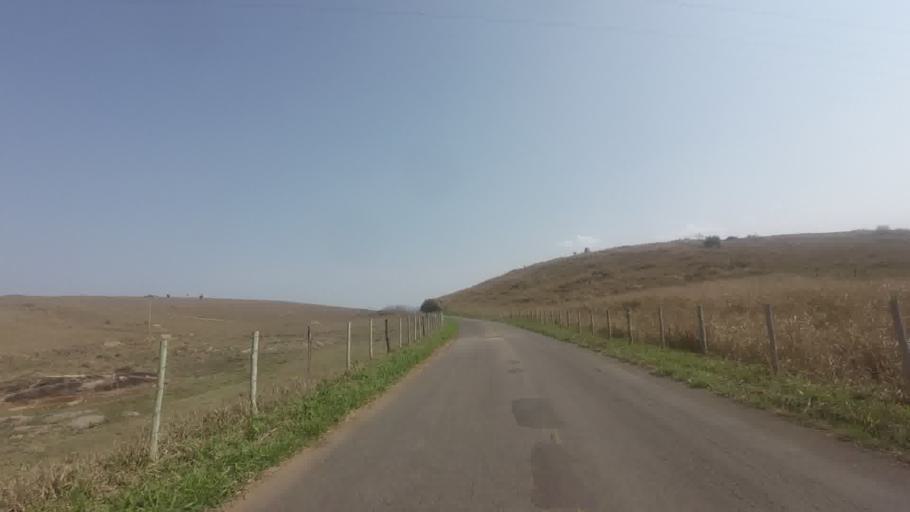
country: BR
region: Rio de Janeiro
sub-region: Bom Jesus Do Itabapoana
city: Bom Jesus do Itabapoana
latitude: -21.1219
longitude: -41.5666
